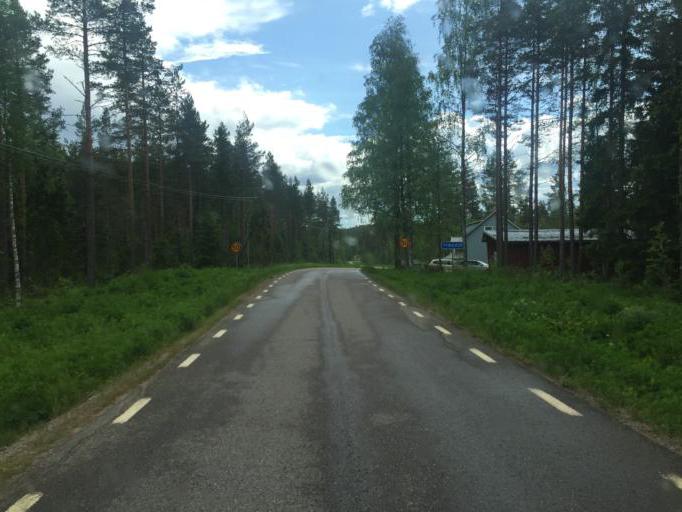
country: SE
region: Vaermland
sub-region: Hagfors Kommun
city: Hagfors
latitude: 60.2963
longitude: 13.8679
